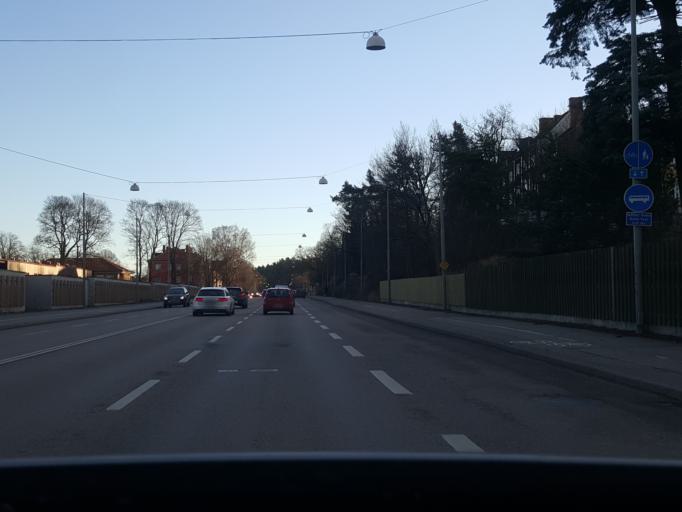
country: SE
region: Stockholm
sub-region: Stockholms Kommun
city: Bromma
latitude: 59.3396
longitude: 17.9630
